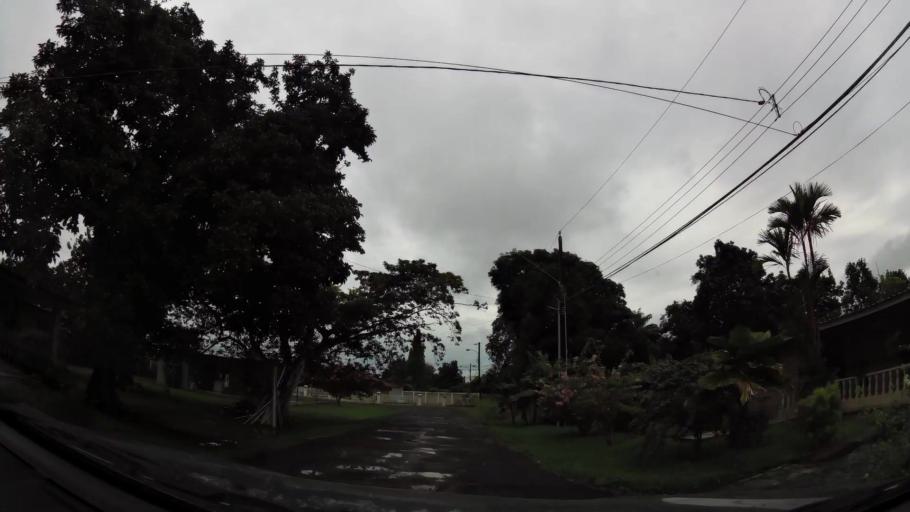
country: PA
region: Chiriqui
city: David
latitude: 8.4251
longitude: -82.4499
